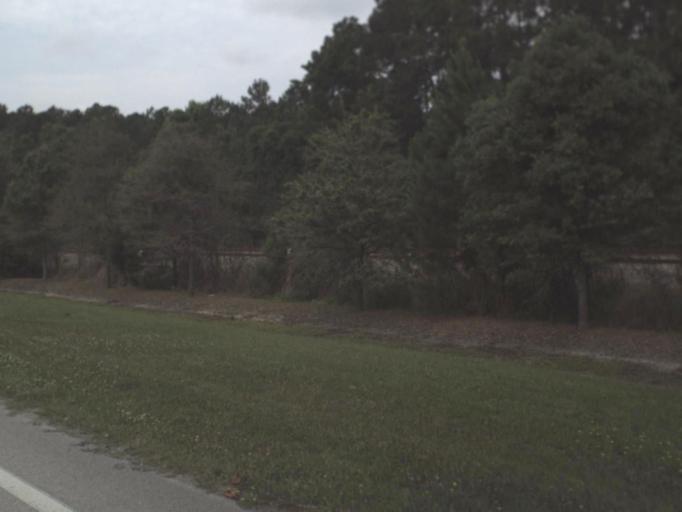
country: US
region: Florida
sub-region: Clay County
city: Orange Park
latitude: 30.2048
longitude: -81.7071
